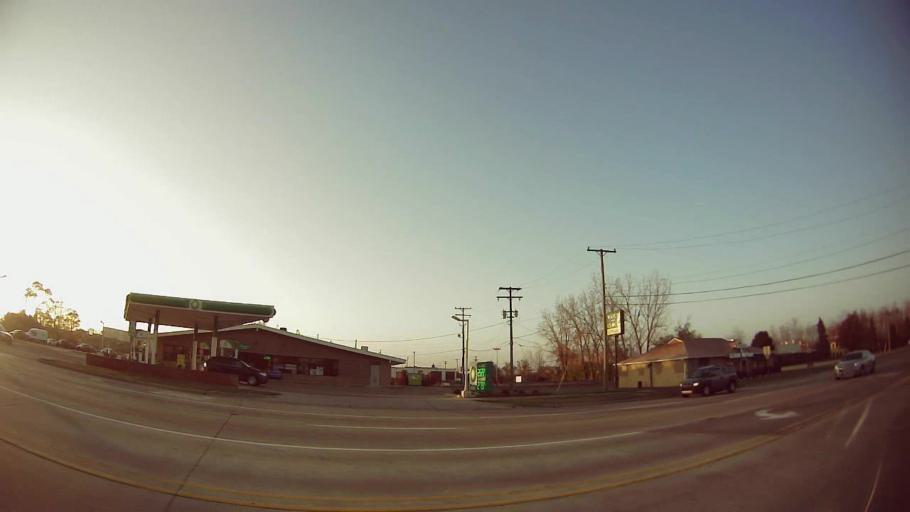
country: US
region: Michigan
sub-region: Oakland County
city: Clawson
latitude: 42.5494
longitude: -83.1082
